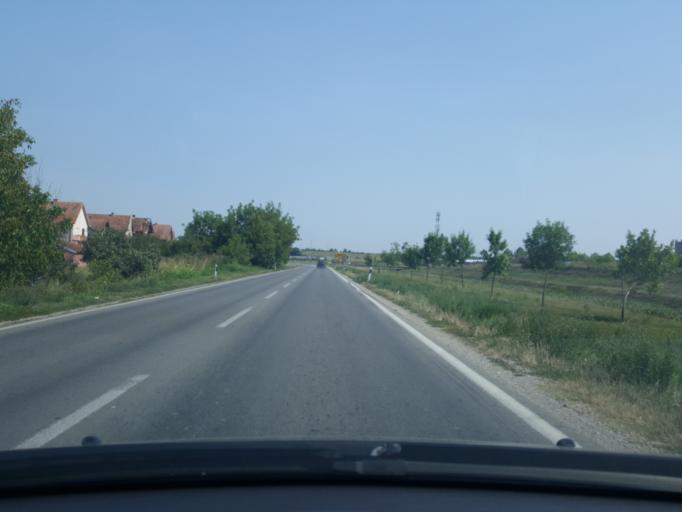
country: RS
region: Central Serbia
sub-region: Macvanski Okrug
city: Sabac
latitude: 44.7425
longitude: 19.6722
